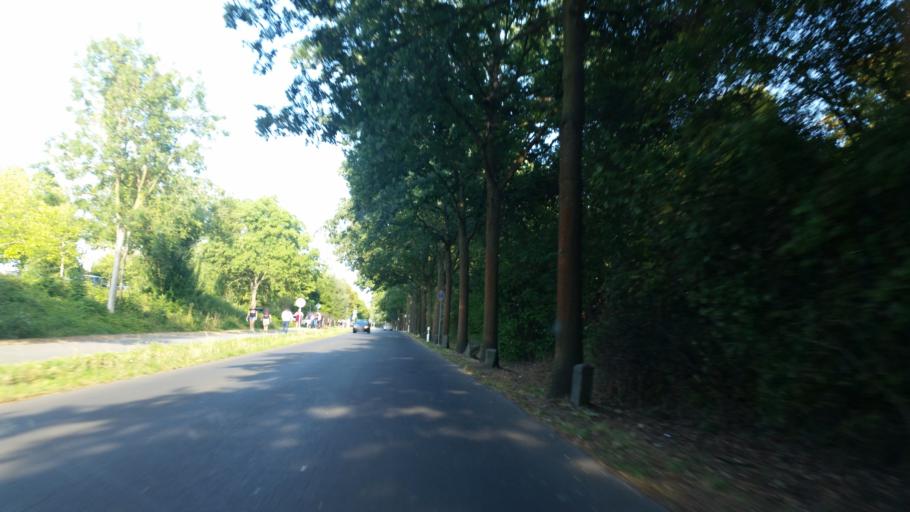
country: DE
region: Hesse
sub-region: Regierungsbezirk Kassel
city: Fuldabruck
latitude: 51.2892
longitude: 9.4951
